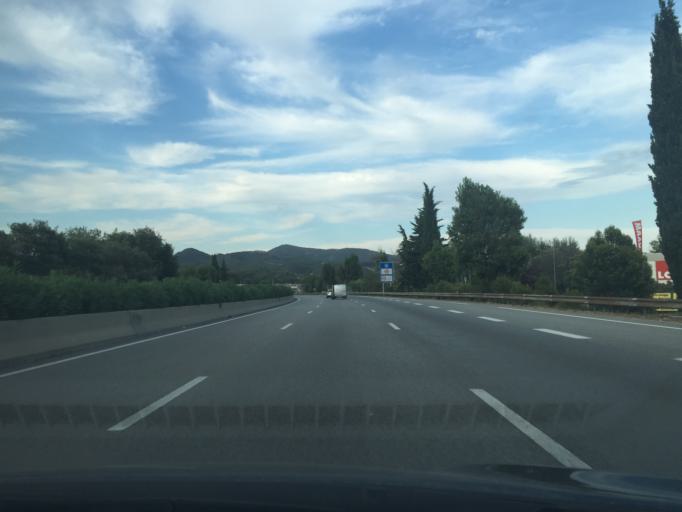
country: FR
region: Provence-Alpes-Cote d'Azur
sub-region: Departement du Var
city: Frejus
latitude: 43.4703
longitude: 6.7346
